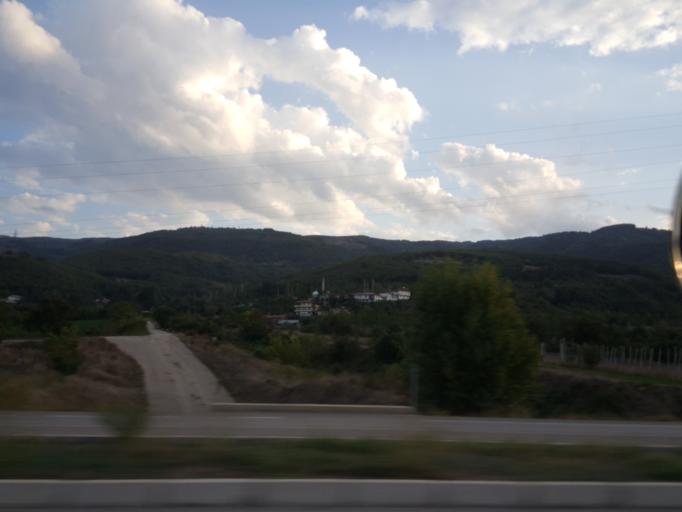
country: TR
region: Tokat
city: Niksar
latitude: 40.4895
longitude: 36.9550
